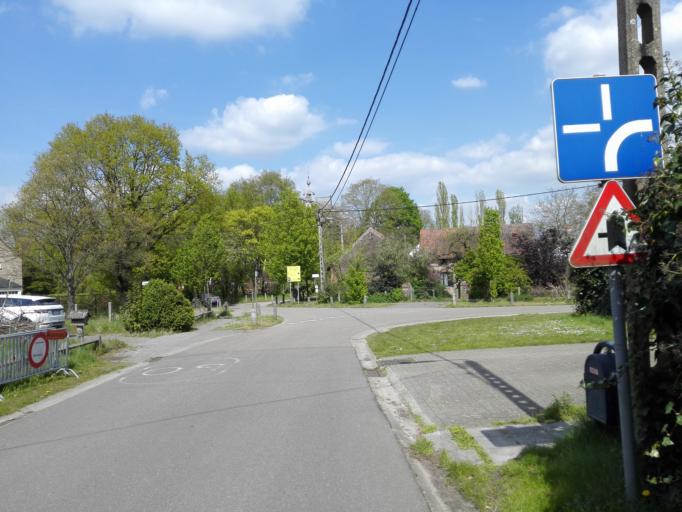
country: BE
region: Flanders
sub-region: Provincie Vlaams-Brabant
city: Rotselaar
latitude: 50.9570
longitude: 4.7205
